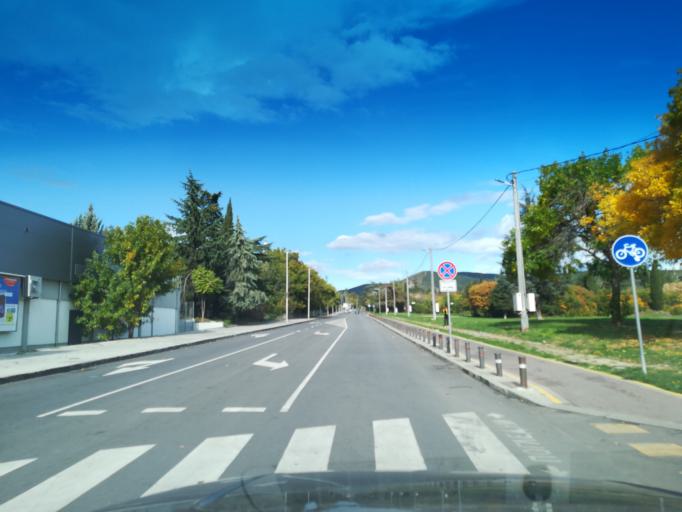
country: BG
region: Stara Zagora
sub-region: Obshtina Stara Zagora
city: Stara Zagora
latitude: 42.4388
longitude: 25.6357
